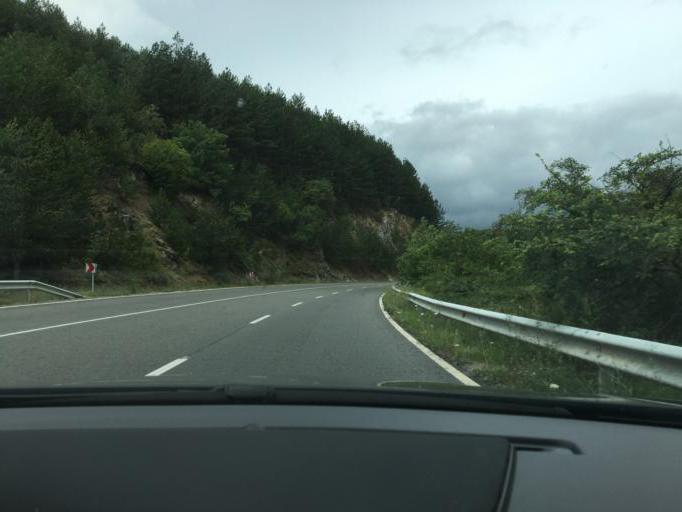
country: BG
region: Kyustendil
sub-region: Obshtina Bobovdol
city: Bobovdol
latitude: 42.2701
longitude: 22.9630
